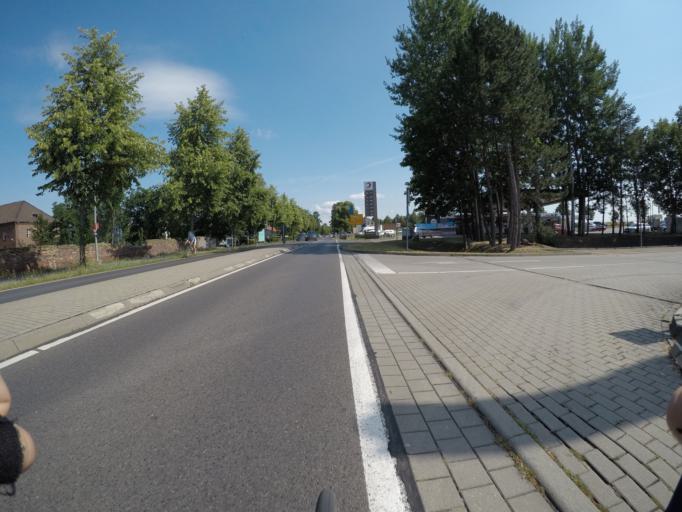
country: DE
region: Brandenburg
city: Bernau bei Berlin
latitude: 52.6678
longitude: 13.5816
